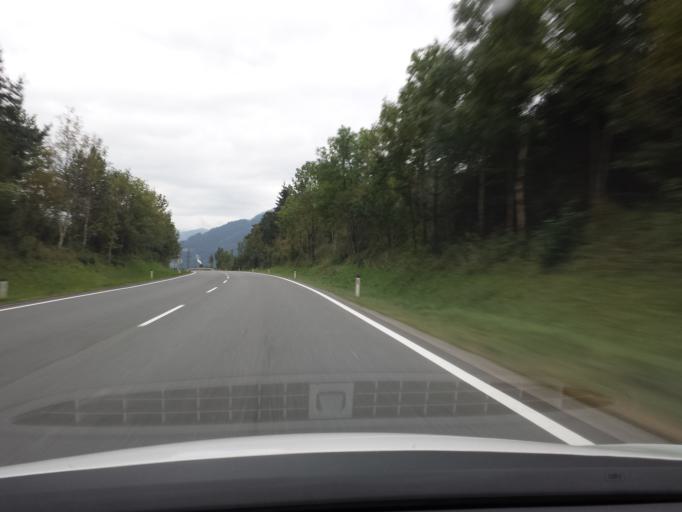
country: AT
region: Salzburg
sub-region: Politischer Bezirk Zell am See
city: Saalfelden am Steinernen Meer
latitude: 47.4696
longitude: 12.8289
